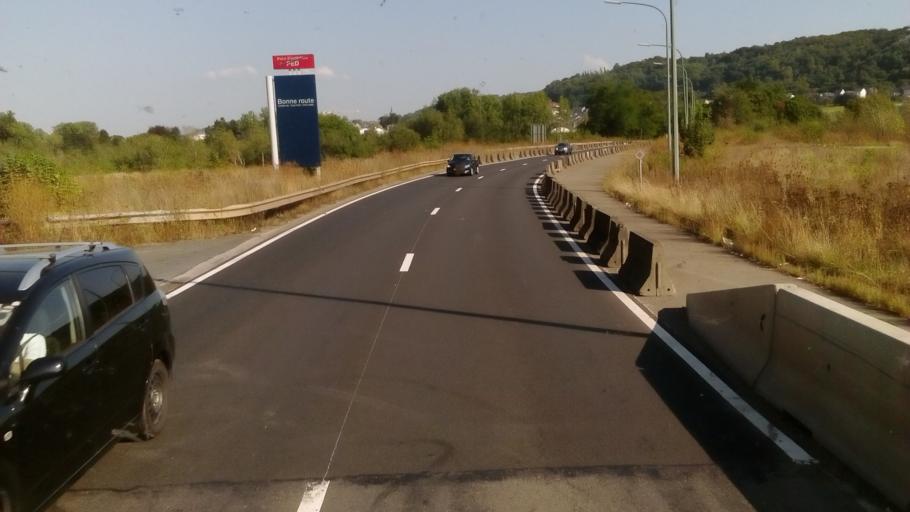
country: FR
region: Lorraine
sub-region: Departement de Meurthe-et-Moselle
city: Saulnes
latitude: 49.5486
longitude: 5.8163
